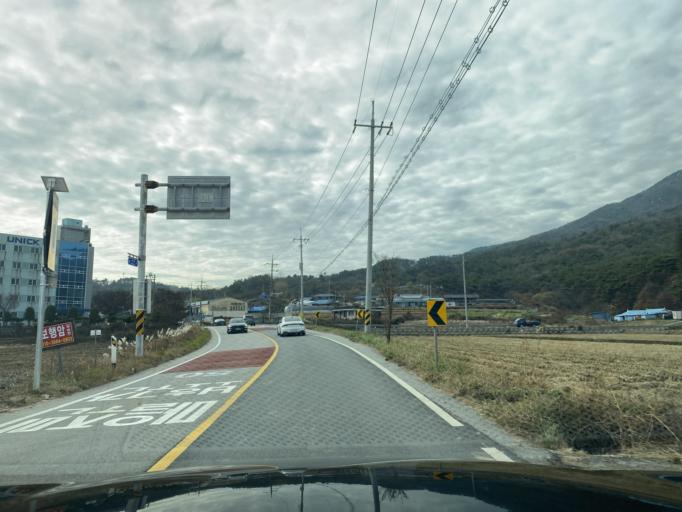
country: KR
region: Chungcheongnam-do
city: Hongsung
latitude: 36.6761
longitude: 126.6430
